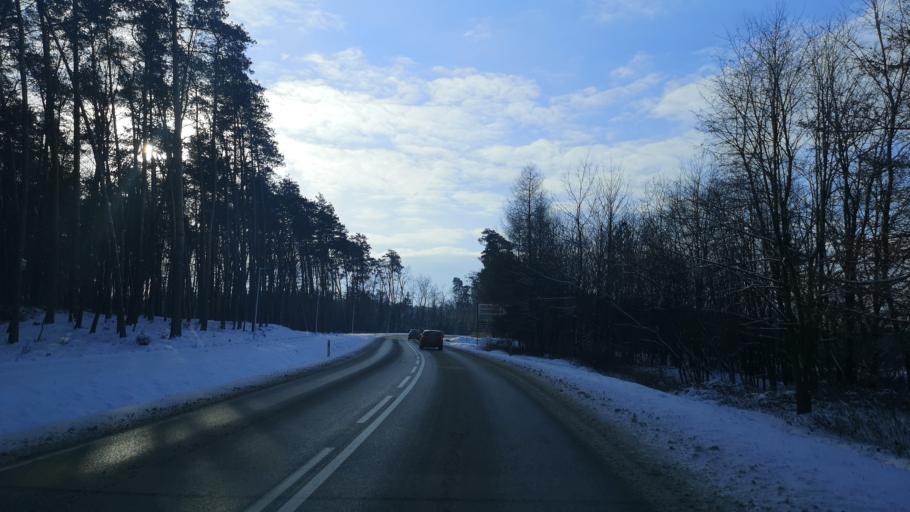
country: PL
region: Subcarpathian Voivodeship
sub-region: Powiat przeworski
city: Tryncza
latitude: 50.1301
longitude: 22.5366
